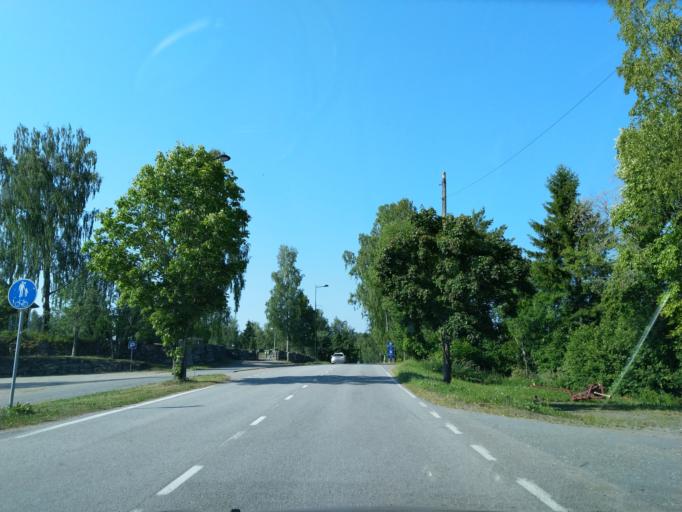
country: FI
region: Satakunta
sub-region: Pori
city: Pomarkku
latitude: 61.6945
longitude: 22.0110
